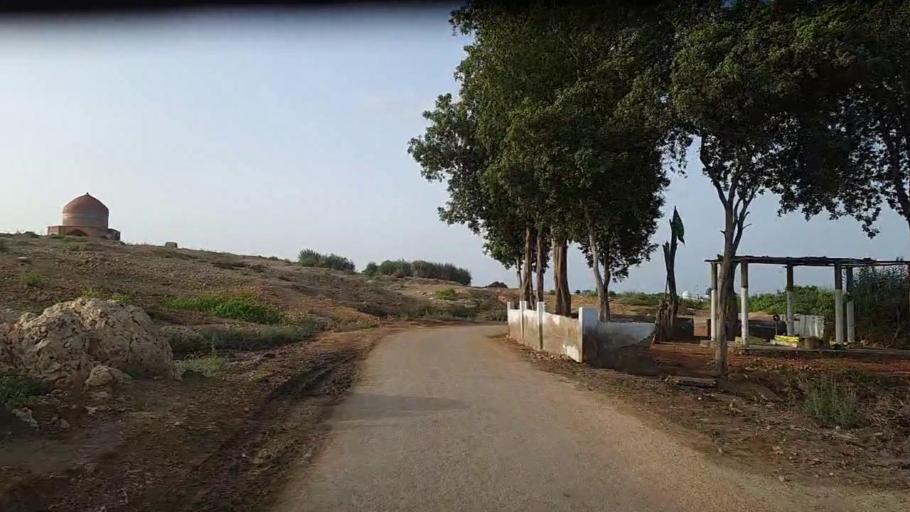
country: PK
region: Sindh
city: Thatta
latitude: 24.7565
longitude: 67.9036
